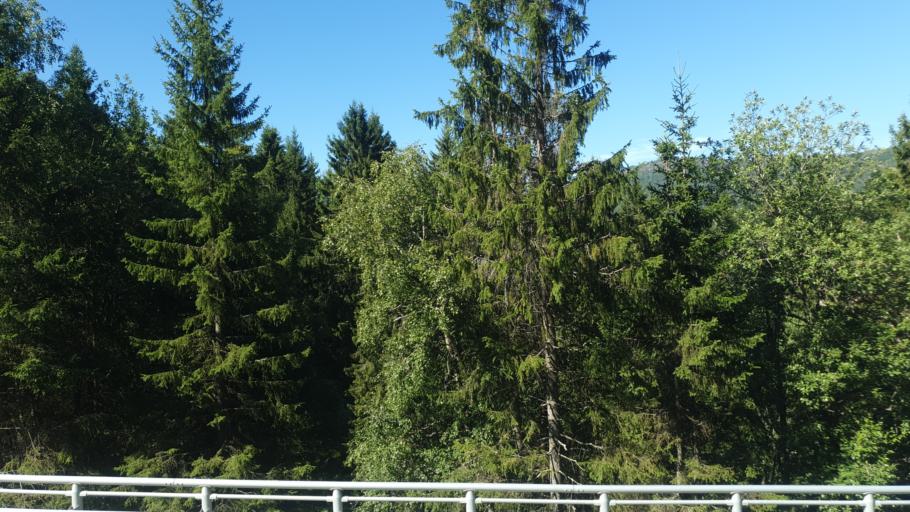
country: NO
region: Sor-Trondelag
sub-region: Meldal
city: Meldal
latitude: 63.1534
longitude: 9.7210
